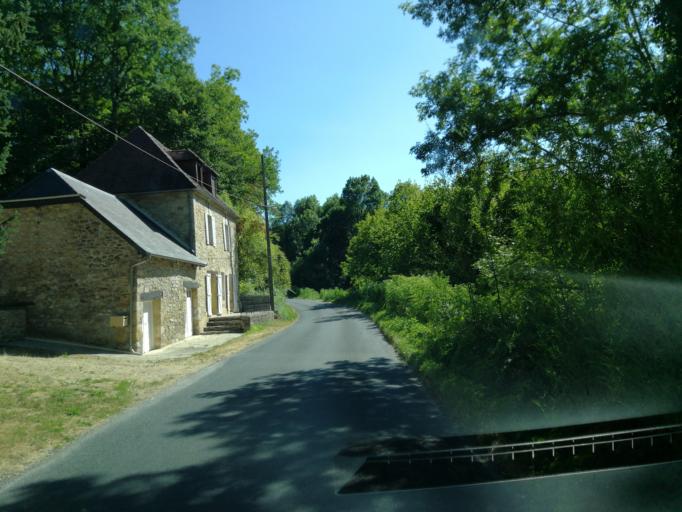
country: FR
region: Aquitaine
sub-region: Departement de la Dordogne
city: Eyvigues-et-Eybenes
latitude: 44.8689
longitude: 1.3783
